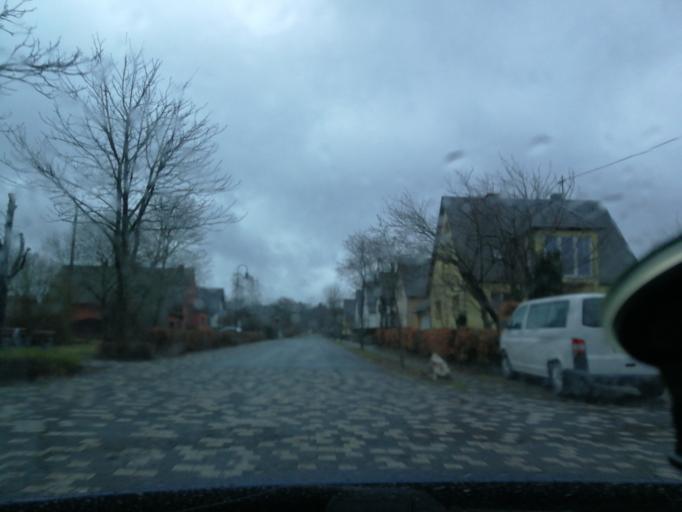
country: DE
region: Rheinland-Pfalz
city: Thalfang
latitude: 49.7439
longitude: 7.0133
